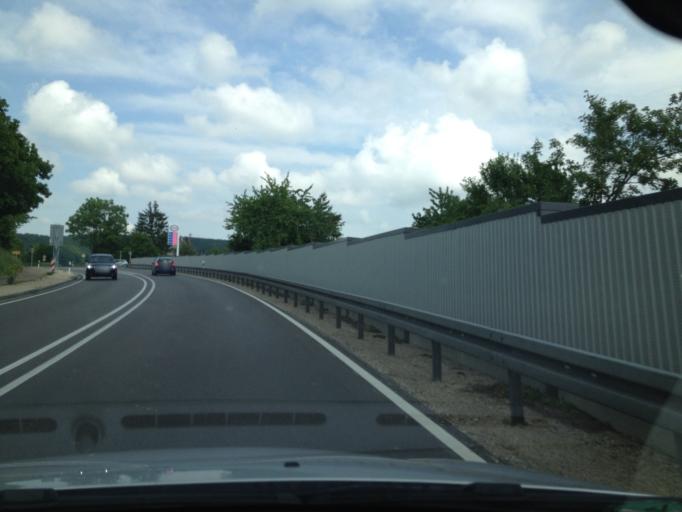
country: DE
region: Bavaria
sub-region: Swabia
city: Harburg
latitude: 48.7878
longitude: 10.6868
